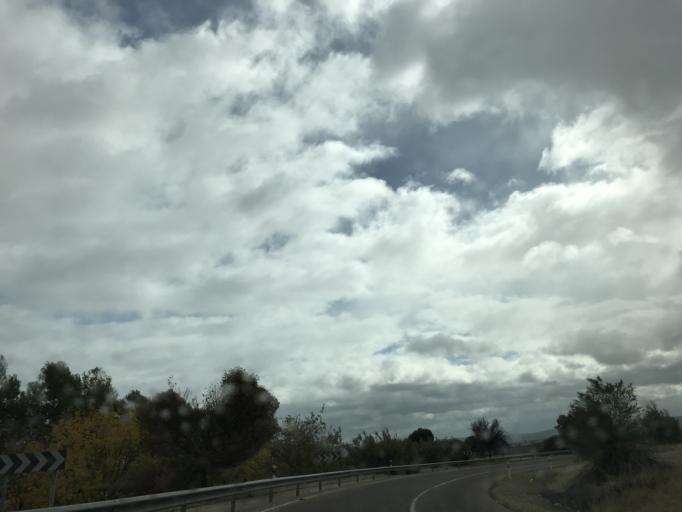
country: ES
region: Andalusia
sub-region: Provincia de Jaen
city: Bailen
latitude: 38.1246
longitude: -3.7586
